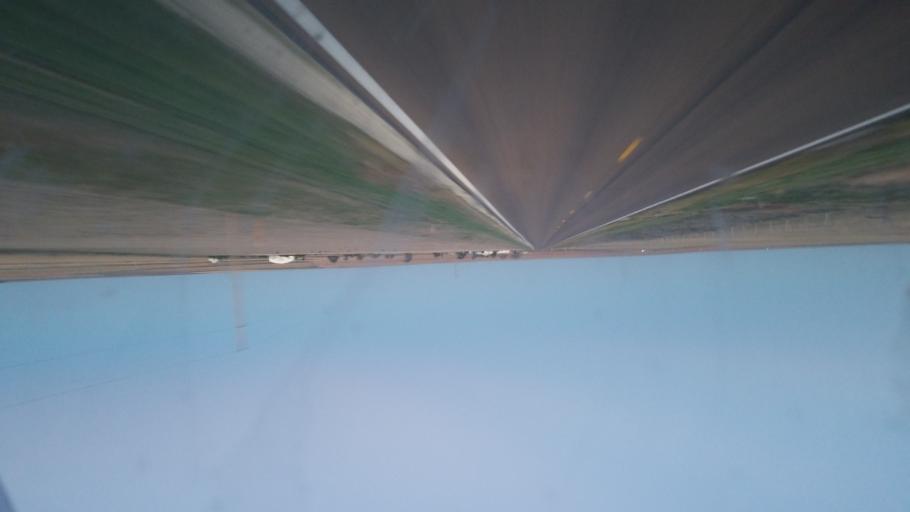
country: US
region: Kansas
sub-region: Wallace County
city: Sharon Springs
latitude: 39.0052
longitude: -101.3825
